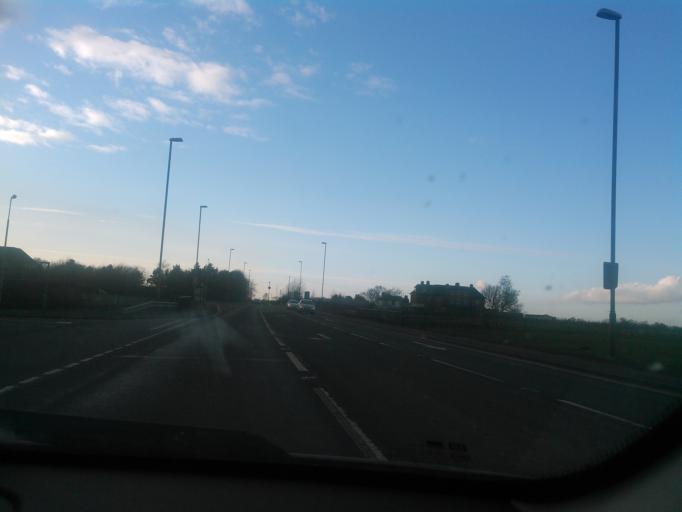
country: GB
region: England
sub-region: Shropshire
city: Stoke upon Tern
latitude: 52.8796
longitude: -2.5305
